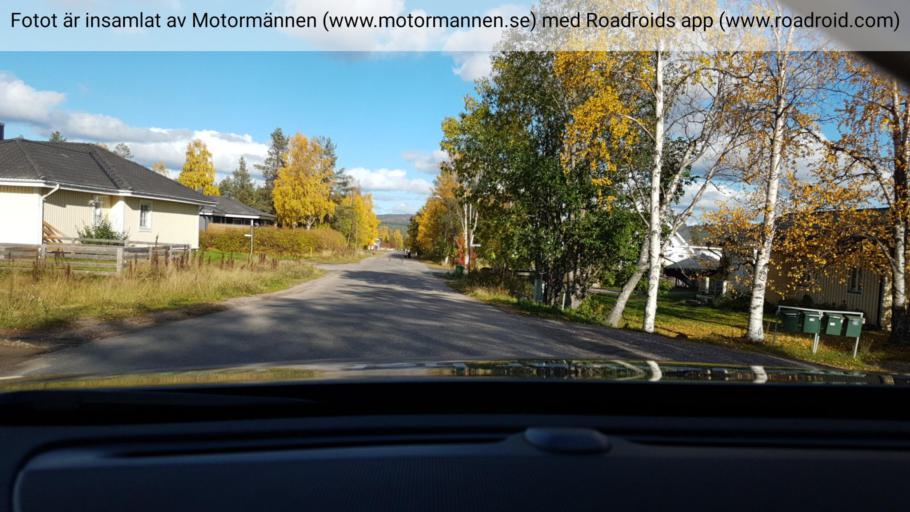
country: SE
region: Norrbotten
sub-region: Gallivare Kommun
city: Malmberget
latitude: 67.1816
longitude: 20.7254
